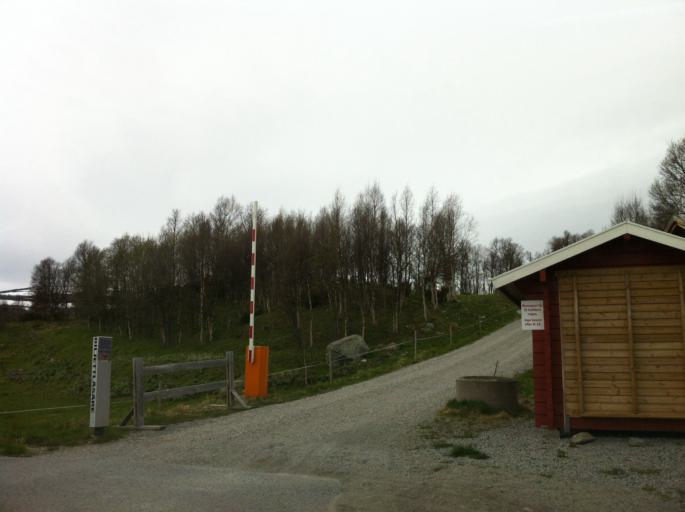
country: NO
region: Sor-Trondelag
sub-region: Tydal
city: Aas
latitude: 62.6392
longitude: 12.4443
